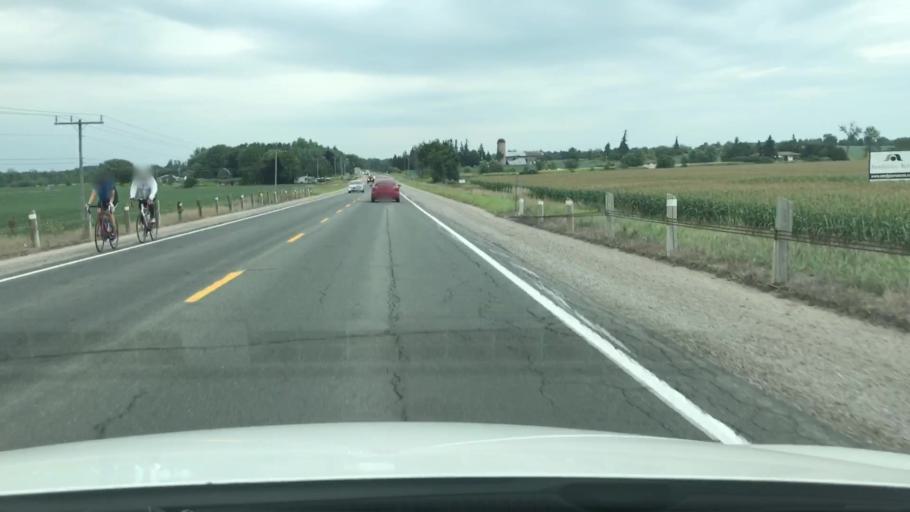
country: CA
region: Ontario
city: Innisfil
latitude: 44.3089
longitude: -79.6154
